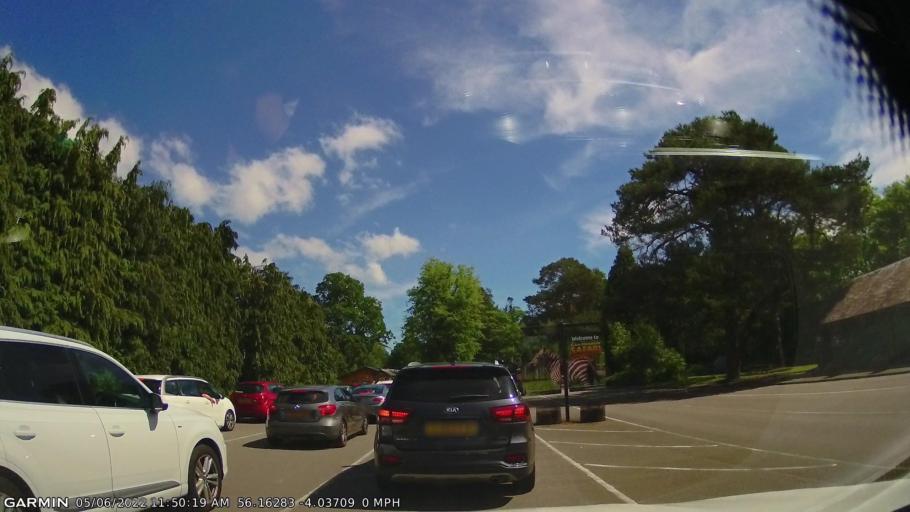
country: GB
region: Scotland
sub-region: Stirling
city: Doune
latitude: 56.1628
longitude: -4.0371
